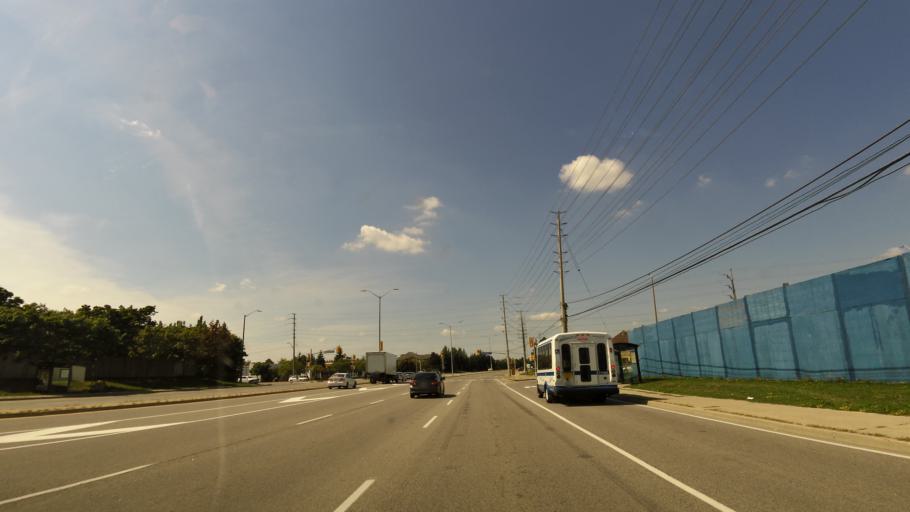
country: CA
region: Ontario
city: Mississauga
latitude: 43.5695
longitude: -79.7215
